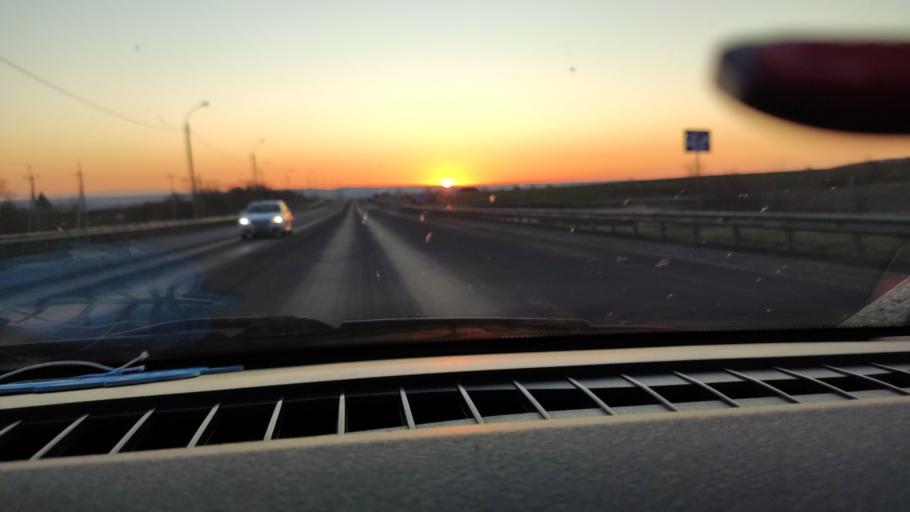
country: RU
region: Saratov
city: Shumeyka
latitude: 51.7894
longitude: 46.1482
